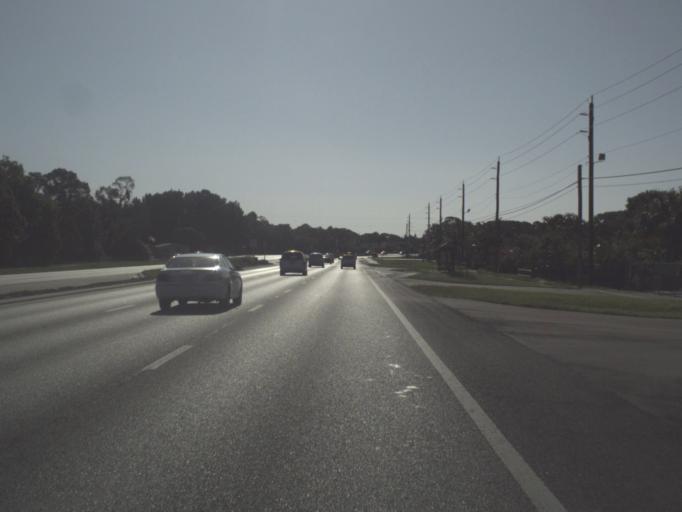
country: US
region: Florida
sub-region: Lee County
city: Estero
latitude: 26.4465
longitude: -81.8159
